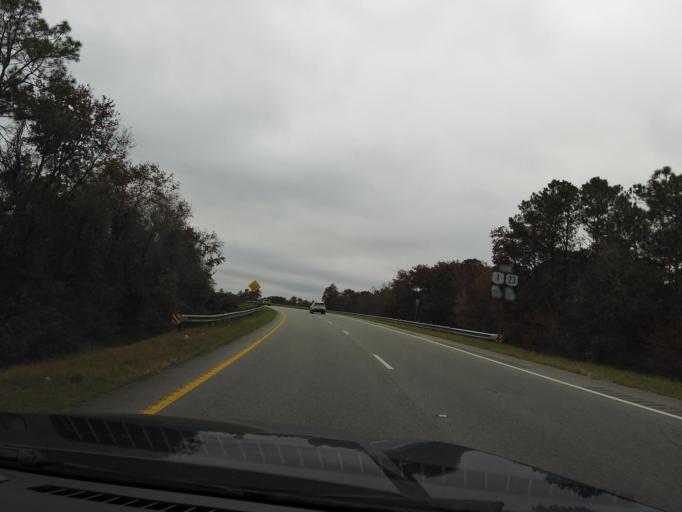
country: US
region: Georgia
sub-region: Charlton County
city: Folkston
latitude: 30.8707
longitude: -82.0135
